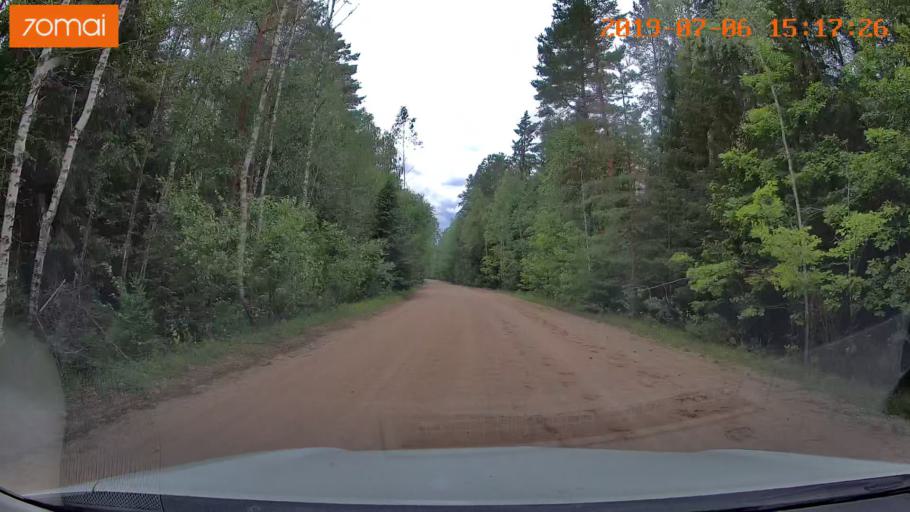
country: BY
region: Minsk
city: Ivyanyets
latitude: 53.9881
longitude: 26.6663
